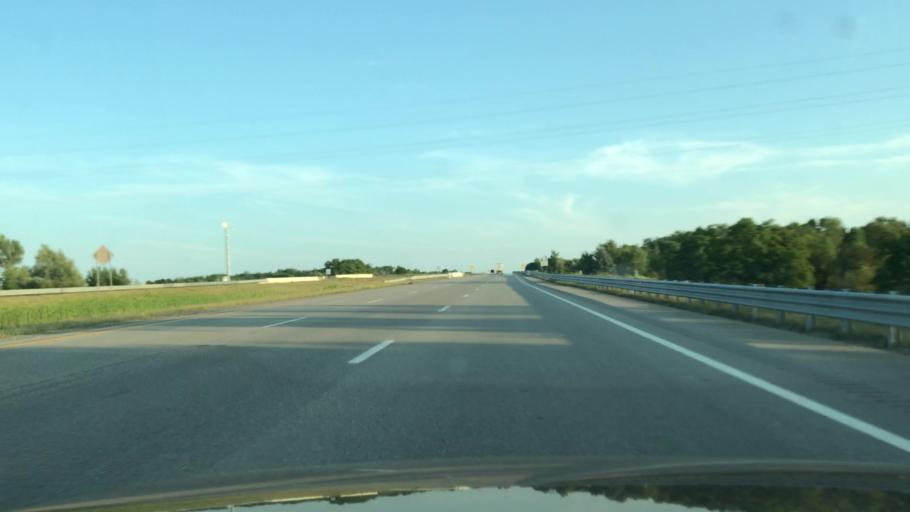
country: US
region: Michigan
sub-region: Osceola County
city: Reed City
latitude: 43.8892
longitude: -85.5282
